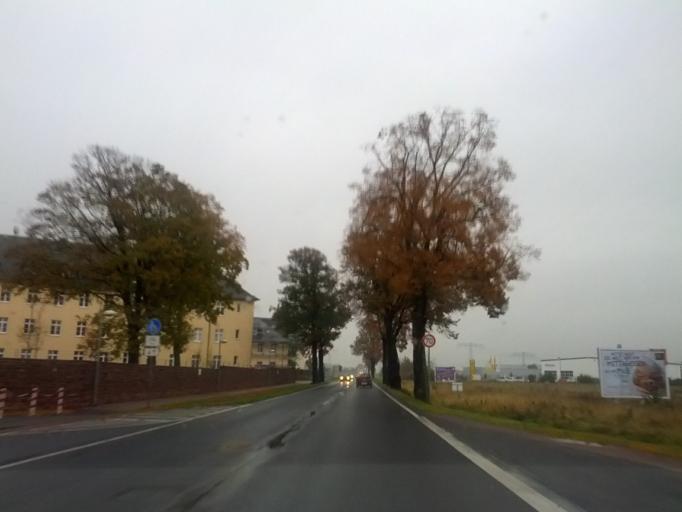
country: DE
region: Thuringia
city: Gotha
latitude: 50.9277
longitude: 10.7181
